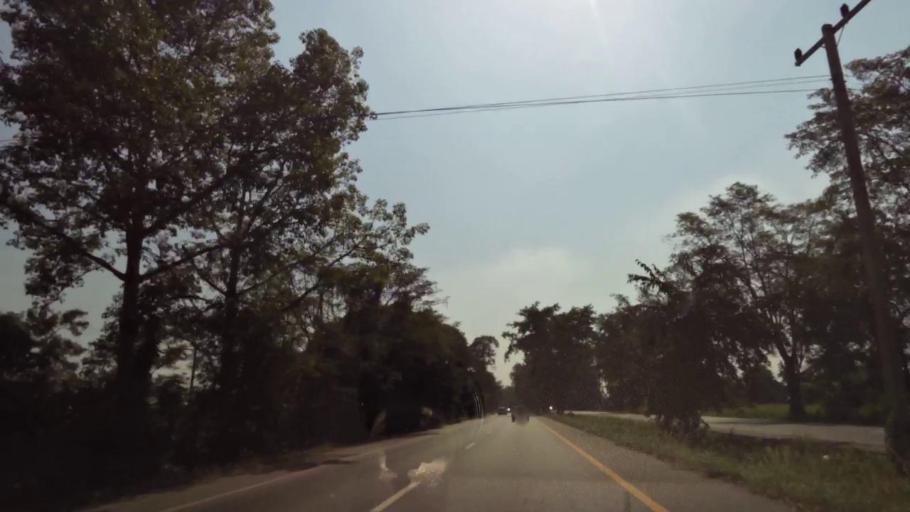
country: TH
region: Phichit
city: Bueng Na Rang
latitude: 16.0270
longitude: 100.1149
